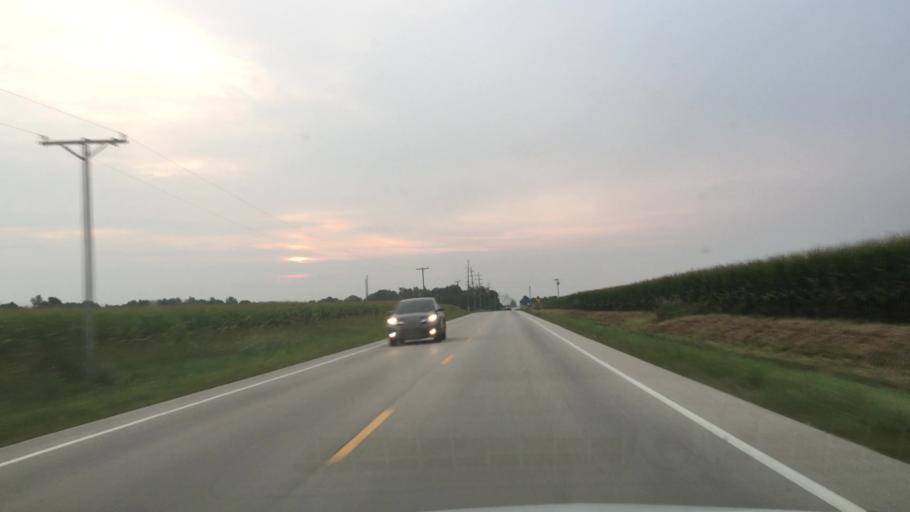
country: US
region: Illinois
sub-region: DeKalb County
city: Waterman
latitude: 41.8490
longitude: -88.7971
